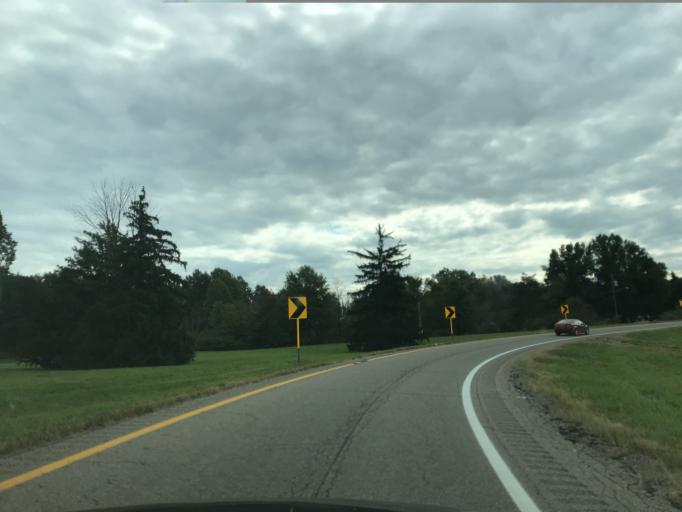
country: US
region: Ohio
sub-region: Trumbull County
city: Howland Center
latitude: 41.2292
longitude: -80.7071
